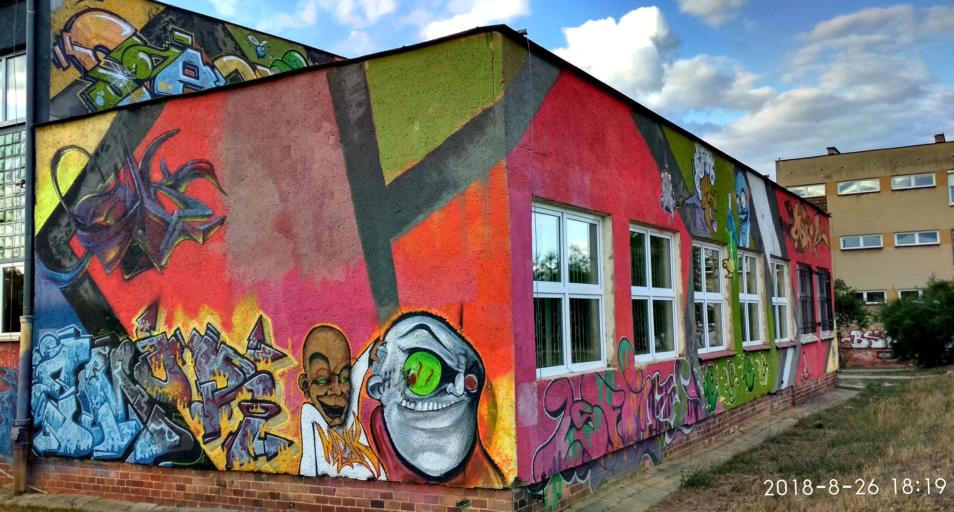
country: PL
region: Lubusz
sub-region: Zielona Gora
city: Zielona Gora
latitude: 51.9342
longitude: 15.4728
